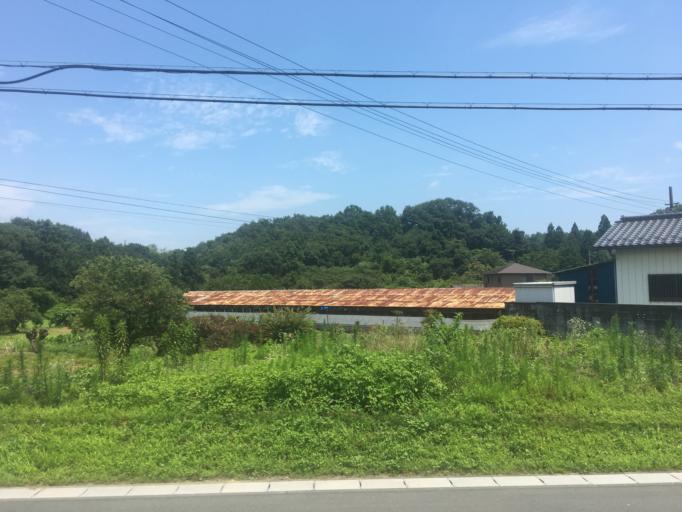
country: JP
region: Saitama
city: Yorii
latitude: 36.0945
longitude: 139.1967
